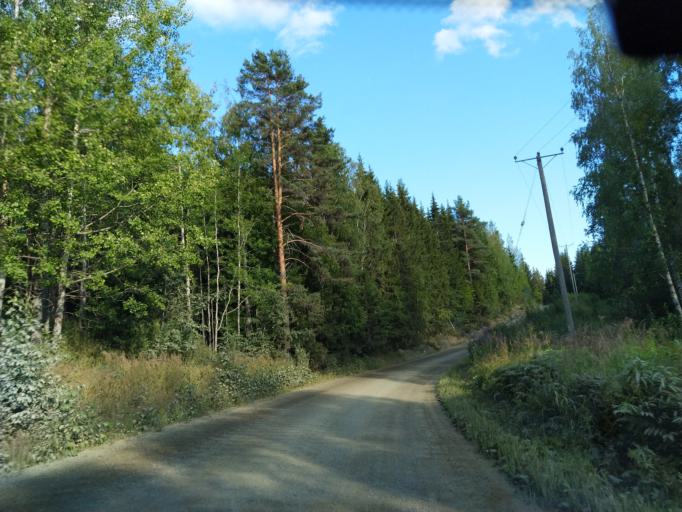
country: FI
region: Central Finland
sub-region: Jaemsae
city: Kuhmoinen
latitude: 61.6938
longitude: 24.9466
